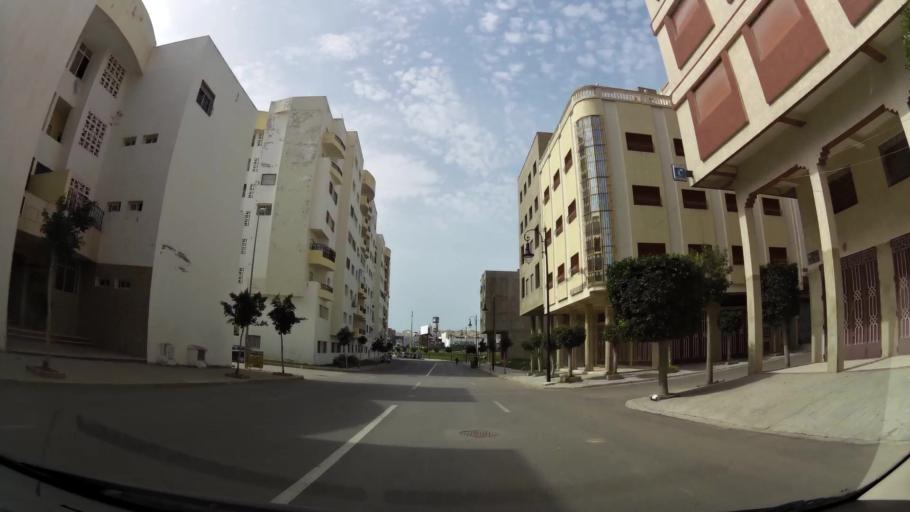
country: MA
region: Tanger-Tetouan
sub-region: Tanger-Assilah
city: Tangier
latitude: 35.7443
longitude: -5.8410
